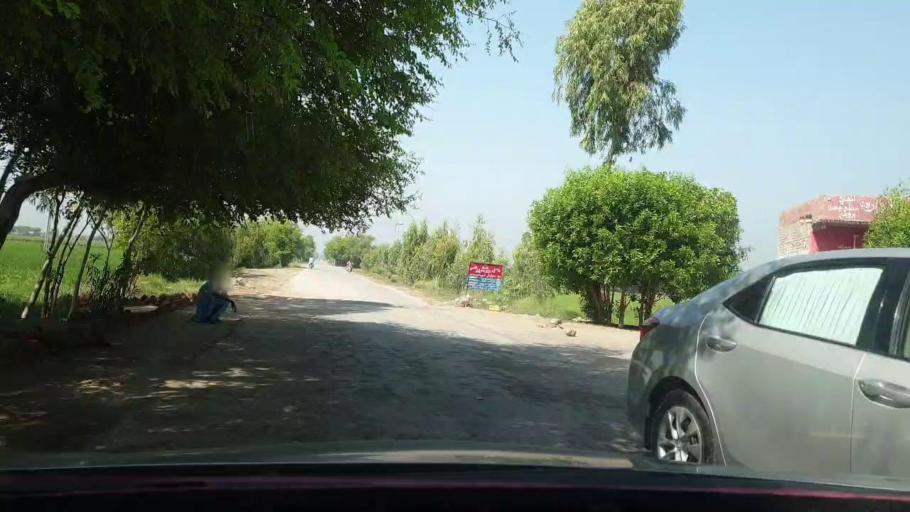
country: PK
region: Sindh
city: Warah
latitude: 27.4644
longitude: 67.8347
